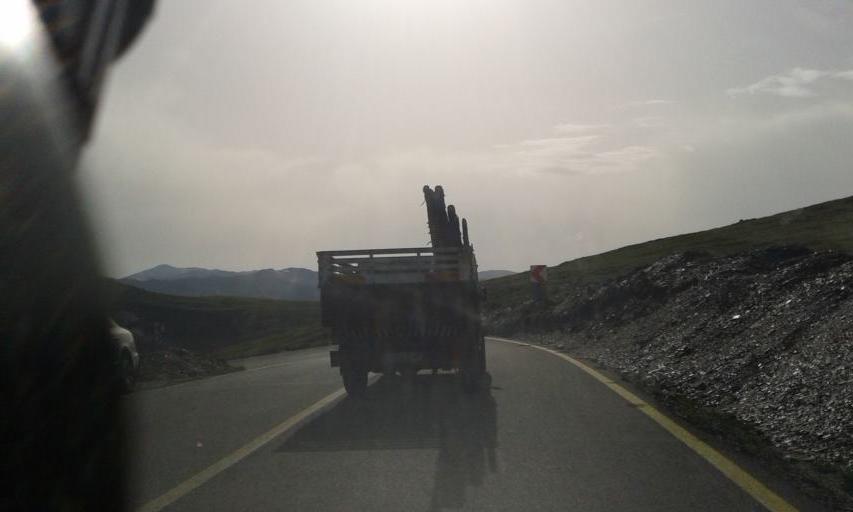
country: RO
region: Gorj
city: Novaci-Straini
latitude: 45.3619
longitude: 23.6572
